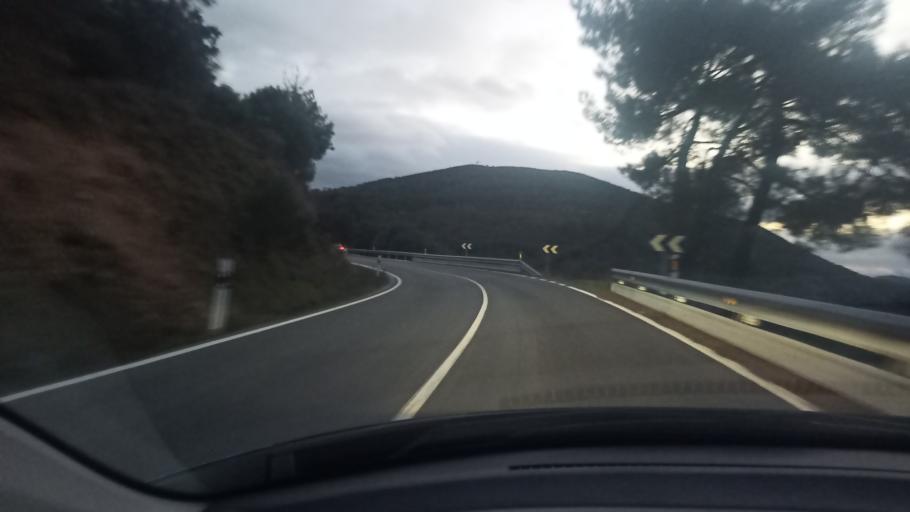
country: ES
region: Madrid
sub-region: Provincia de Madrid
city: Robledo de Chavela
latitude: 40.4679
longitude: -4.2613
